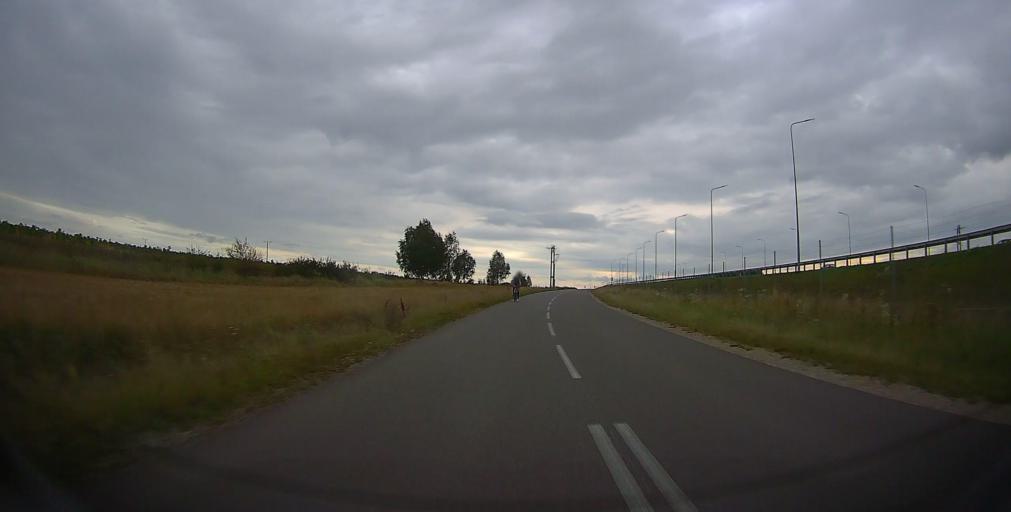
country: PL
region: Masovian Voivodeship
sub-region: Powiat radomski
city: Zakrzew
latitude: 51.4235
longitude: 21.0326
